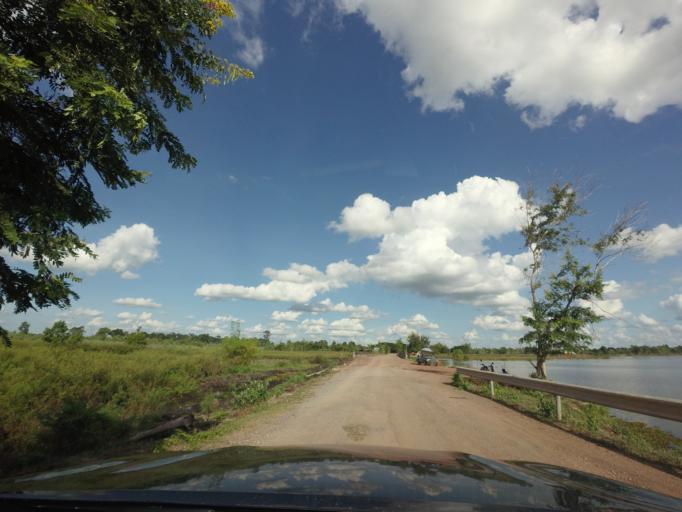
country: TH
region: Changwat Udon Thani
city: Ban Dung
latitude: 17.7503
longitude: 103.3612
